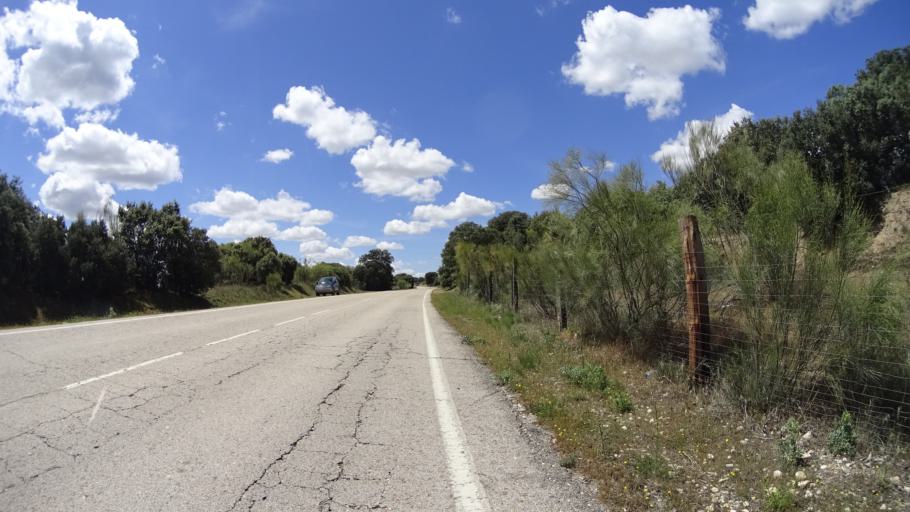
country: ES
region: Madrid
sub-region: Provincia de Madrid
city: Villanueva del Pardillo
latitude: 40.4558
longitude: -3.9493
